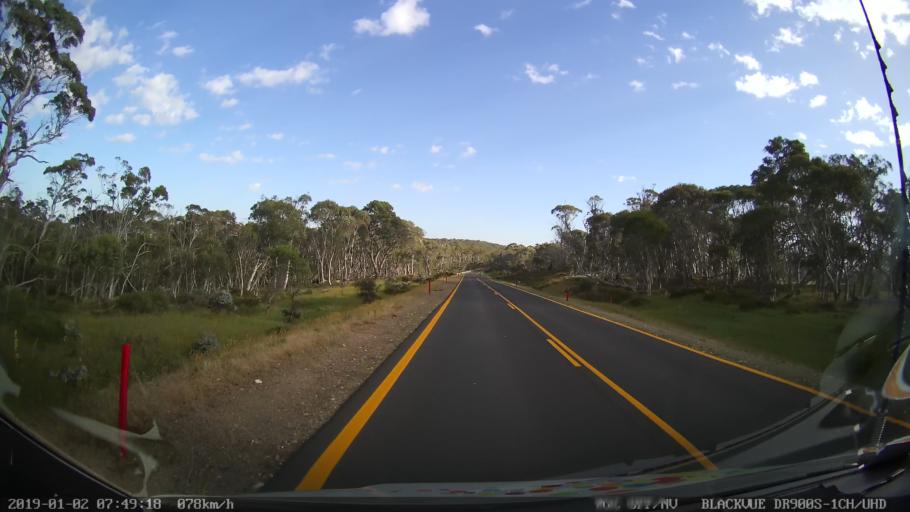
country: AU
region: New South Wales
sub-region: Tumut Shire
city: Tumut
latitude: -35.7433
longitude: 148.5221
